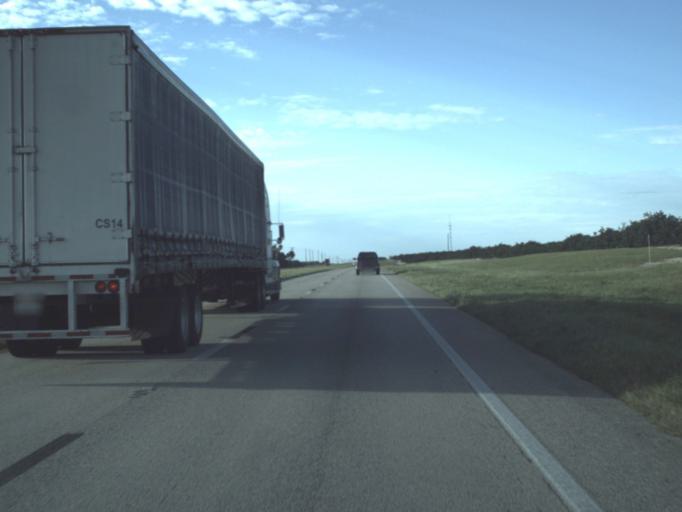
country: US
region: Florida
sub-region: Highlands County
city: Lake Placid
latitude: 27.2274
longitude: -81.3288
